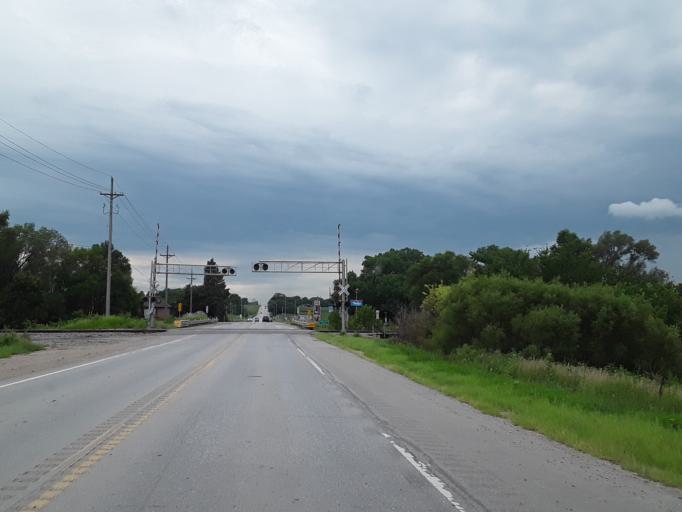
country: US
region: Nebraska
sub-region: Saunders County
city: Yutan
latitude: 41.2338
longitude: -96.3918
